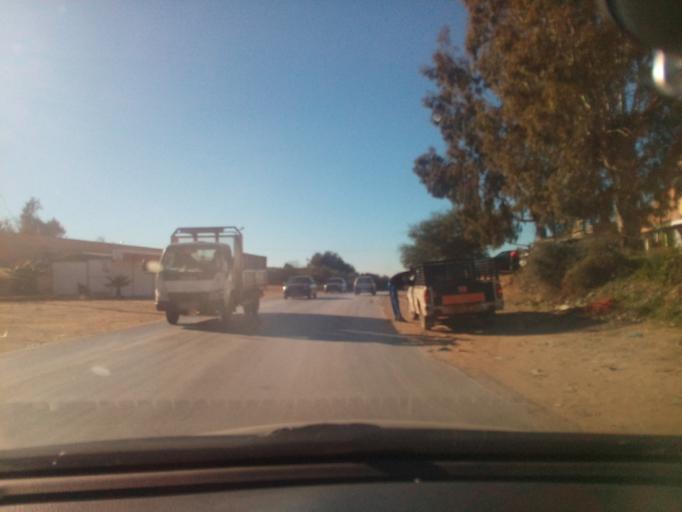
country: DZ
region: Mostaganem
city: Mostaganem
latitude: 35.8965
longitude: 0.2578
